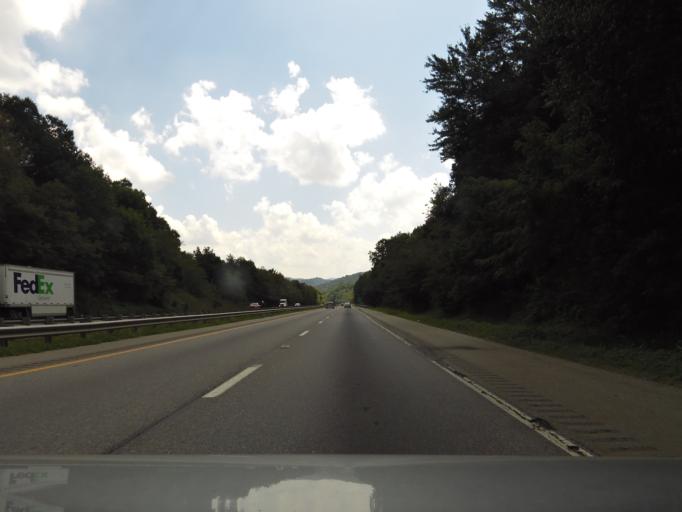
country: US
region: North Carolina
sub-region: Haywood County
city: Cove Creek
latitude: 35.5779
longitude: -82.9826
